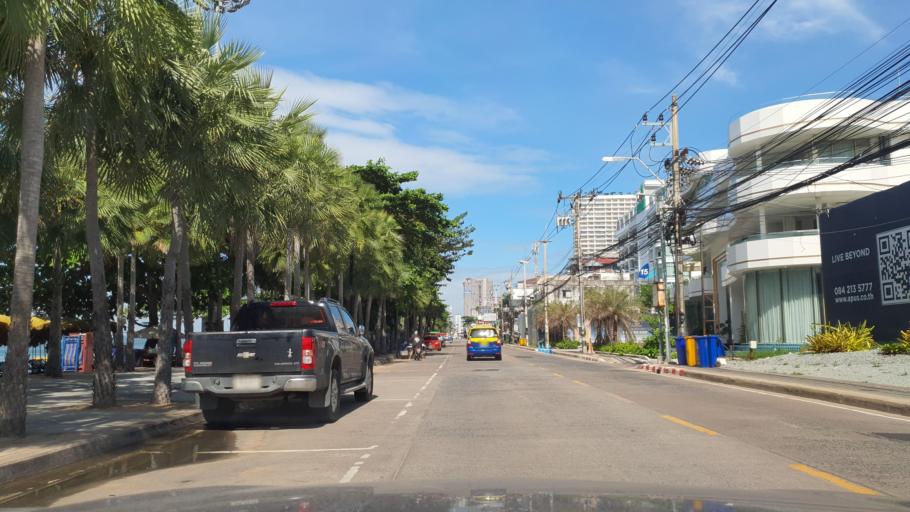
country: TH
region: Chon Buri
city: Phatthaya
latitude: 12.8749
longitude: 100.8869
